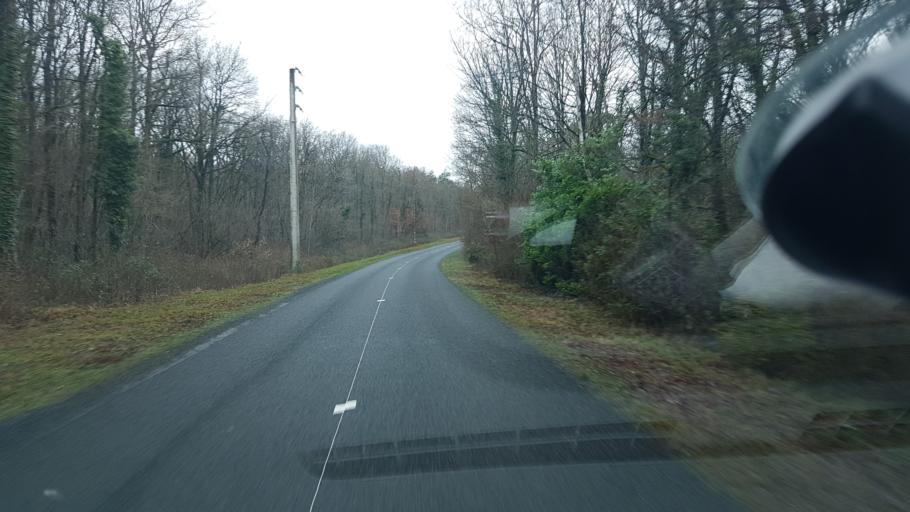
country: FR
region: Ile-de-France
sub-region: Departement de Seine-et-Marne
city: Montigny-sur-Loing
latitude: 48.2756
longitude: 2.7776
